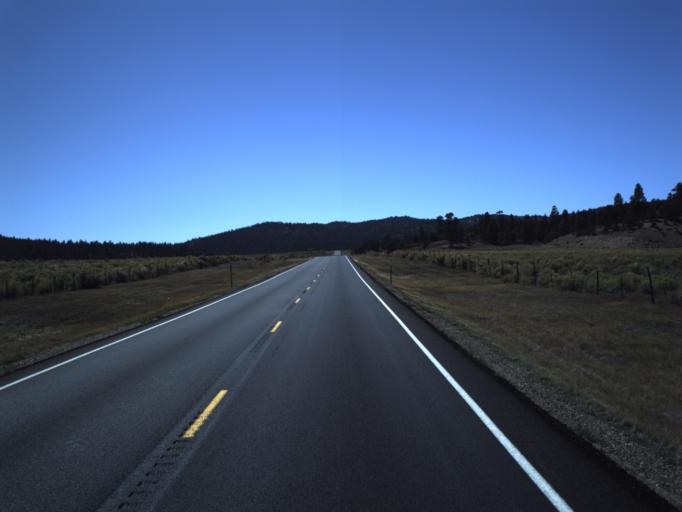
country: US
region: Utah
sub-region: Garfield County
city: Panguitch
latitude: 37.6839
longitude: -111.8116
